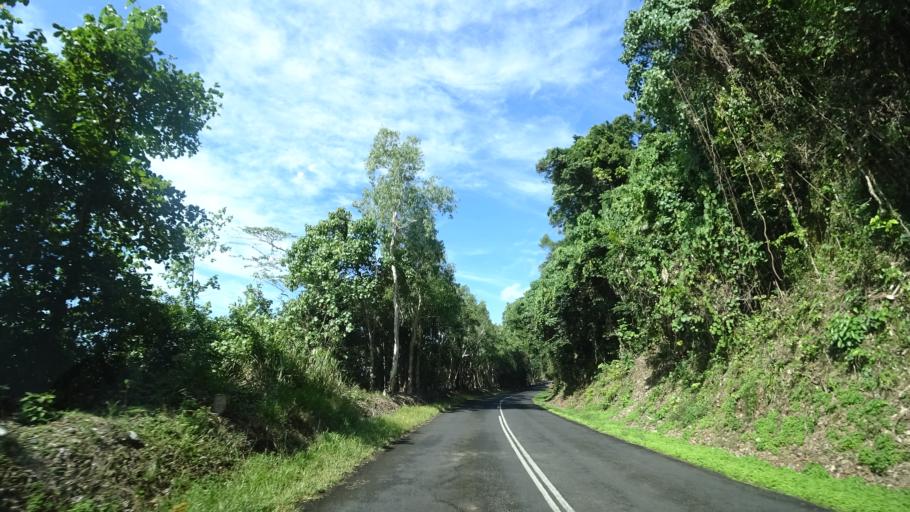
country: AU
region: Queensland
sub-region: Cairns
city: Port Douglas
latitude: -16.1641
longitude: 145.4430
